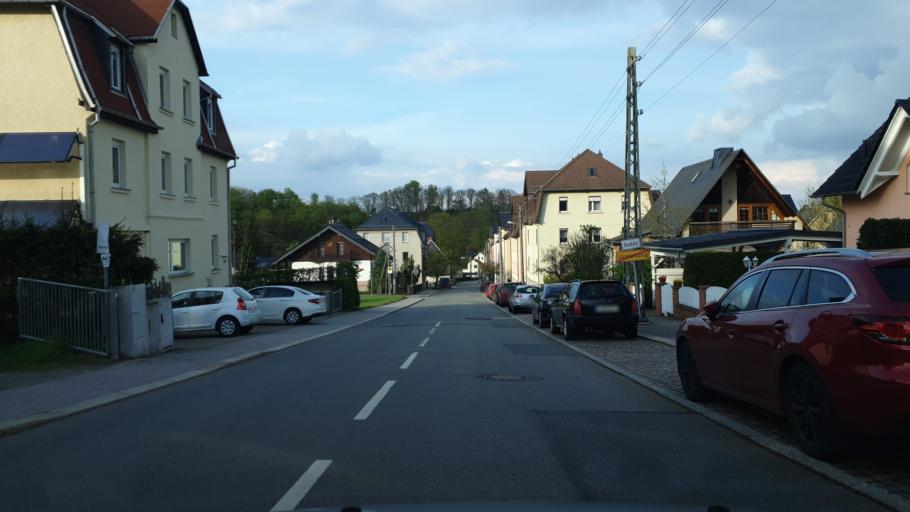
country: DE
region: Saxony
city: Lichtenstein
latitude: 50.7427
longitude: 12.6535
